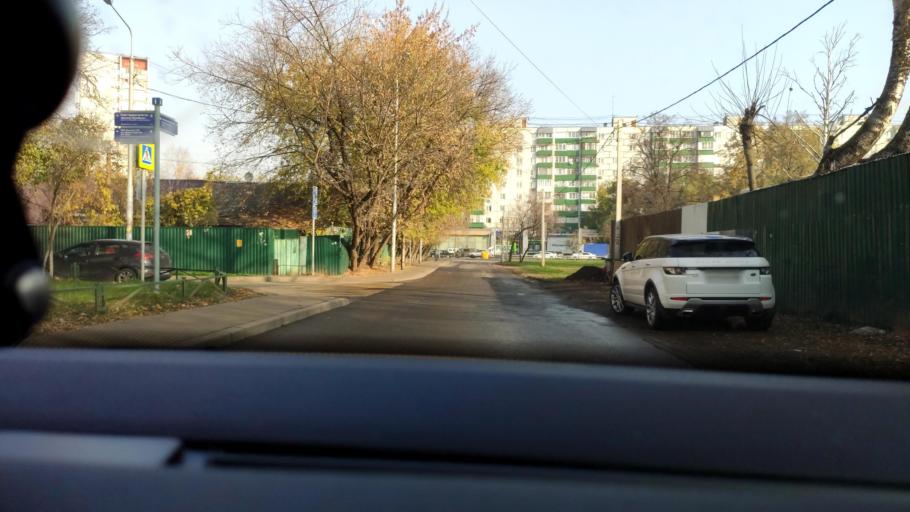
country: RU
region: Moscow
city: Zhulebino
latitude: 55.6955
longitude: 37.8593
